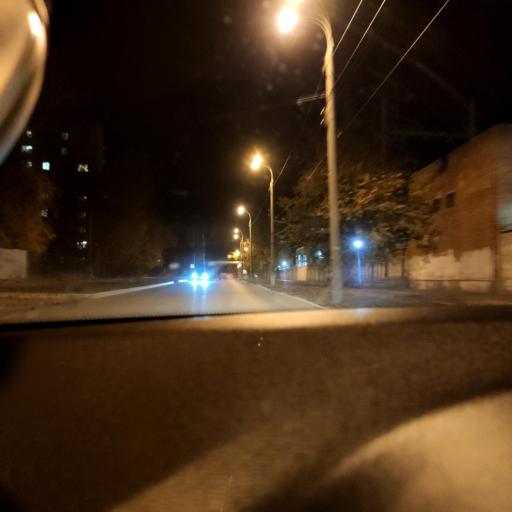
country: RU
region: Samara
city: Samara
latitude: 53.2147
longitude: 50.2048
